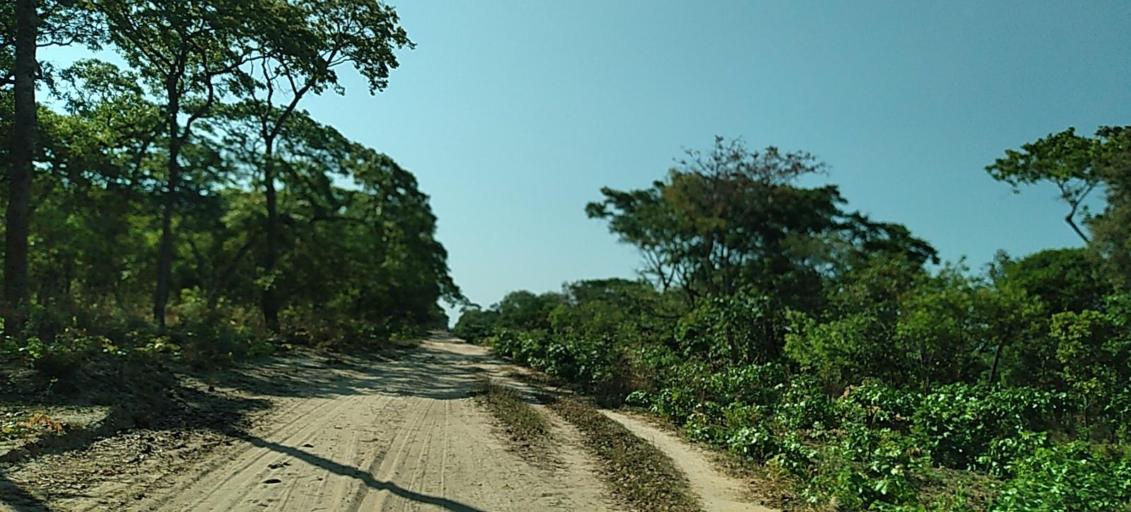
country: ZM
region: Central
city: Mkushi
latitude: -13.4758
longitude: 28.9210
